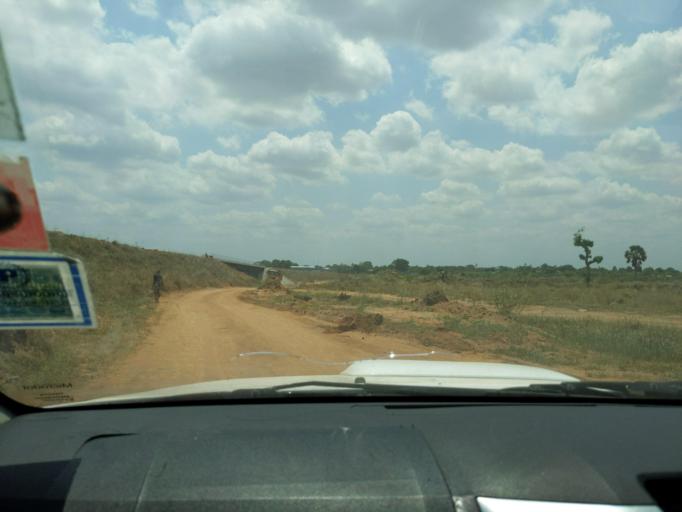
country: MZ
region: Zambezia
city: Quelimane
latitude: -17.2571
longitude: 37.0736
